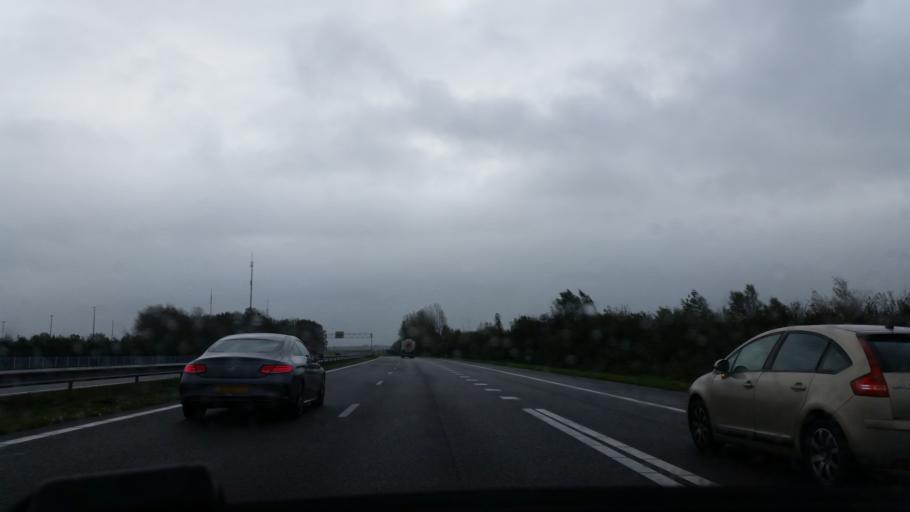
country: NL
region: Friesland
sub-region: Gemeente Boarnsterhim
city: Grou
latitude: 53.0866
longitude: 5.8249
